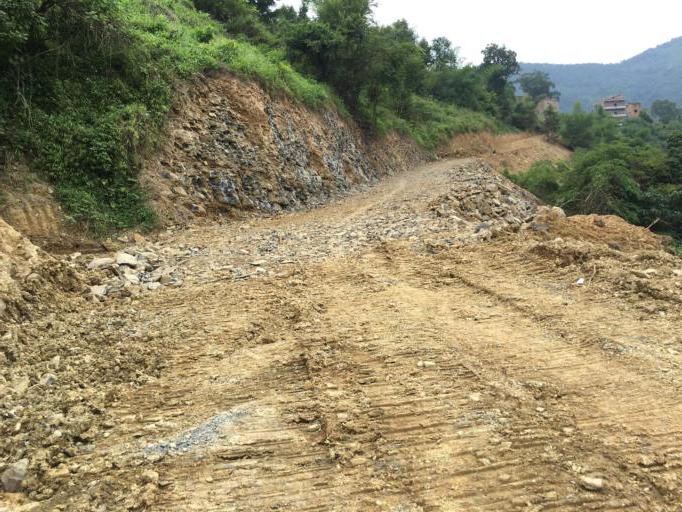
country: CN
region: Guangxi Zhuangzu Zizhiqu
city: Tongle
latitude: 25.1223
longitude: 106.4230
